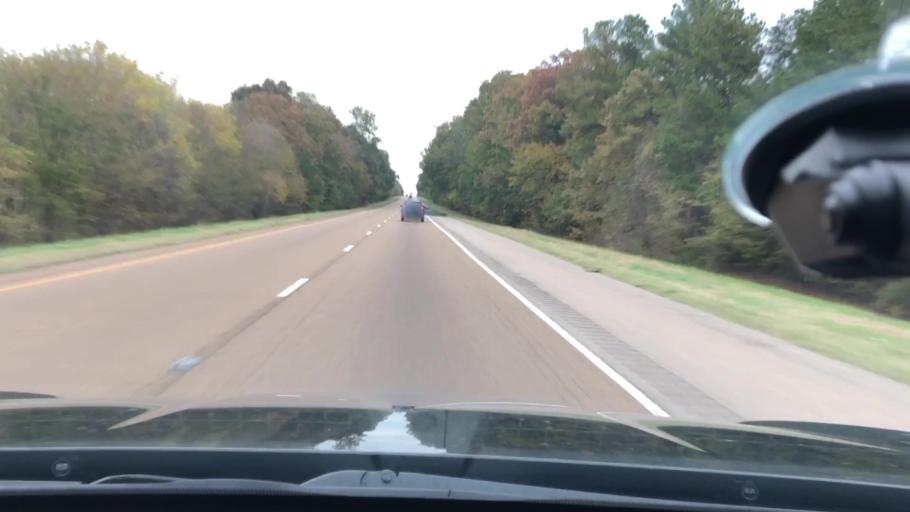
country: US
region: Arkansas
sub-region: Nevada County
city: Prescott
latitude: 33.7844
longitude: -93.4587
